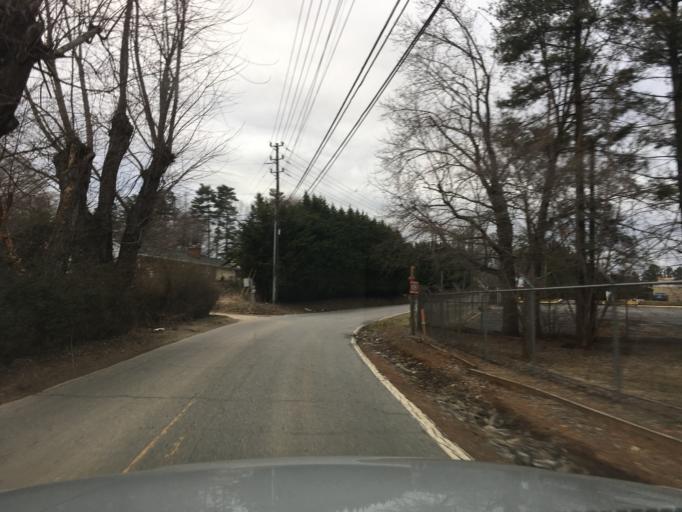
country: US
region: North Carolina
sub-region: Buncombe County
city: Asheville
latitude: 35.6012
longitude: -82.5853
